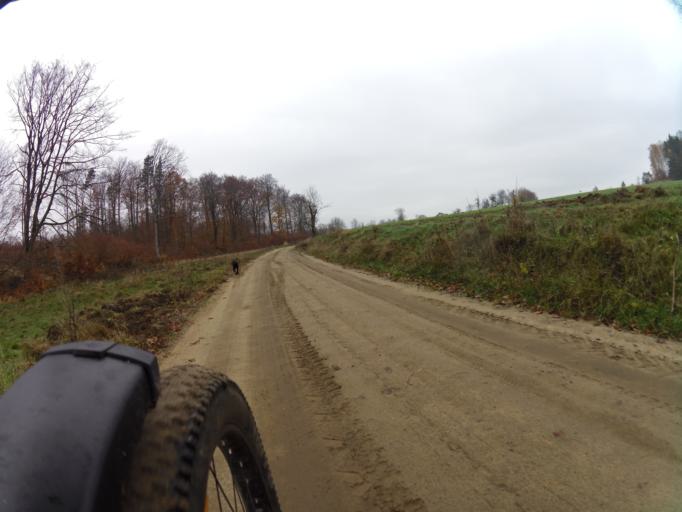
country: PL
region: Pomeranian Voivodeship
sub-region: Powiat pucki
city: Krokowa
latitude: 54.7153
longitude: 18.1394
